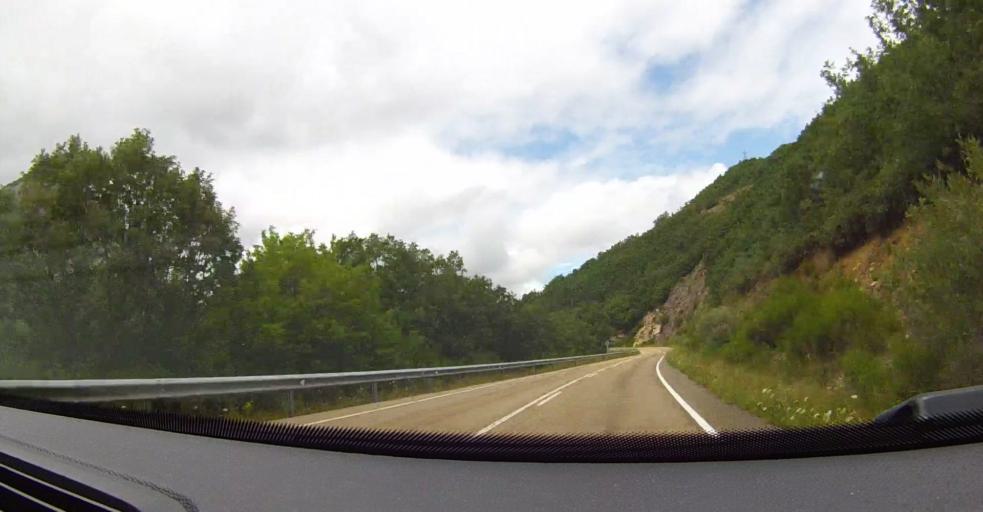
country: ES
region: Castille and Leon
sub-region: Provincia de Leon
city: Reyero
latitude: 42.9512
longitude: -5.2473
